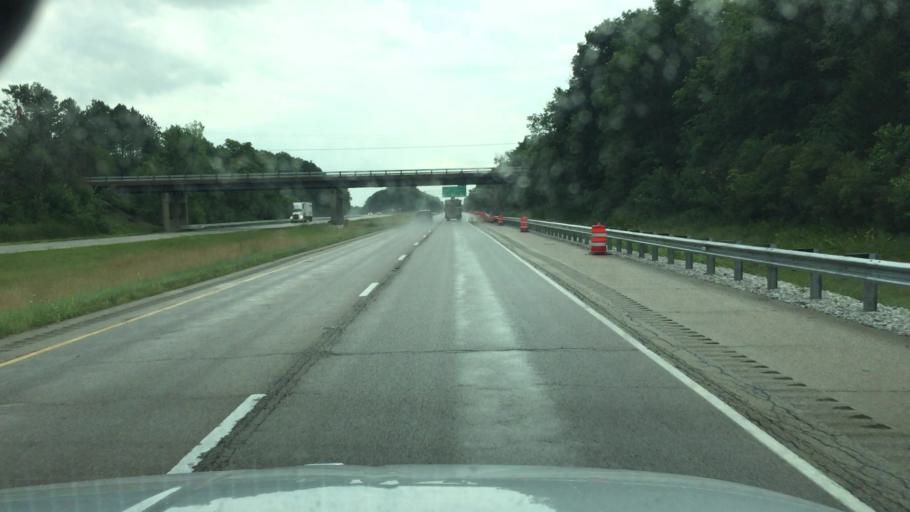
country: US
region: Illinois
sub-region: Peoria County
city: Bellevue
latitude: 40.7484
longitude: -89.6885
